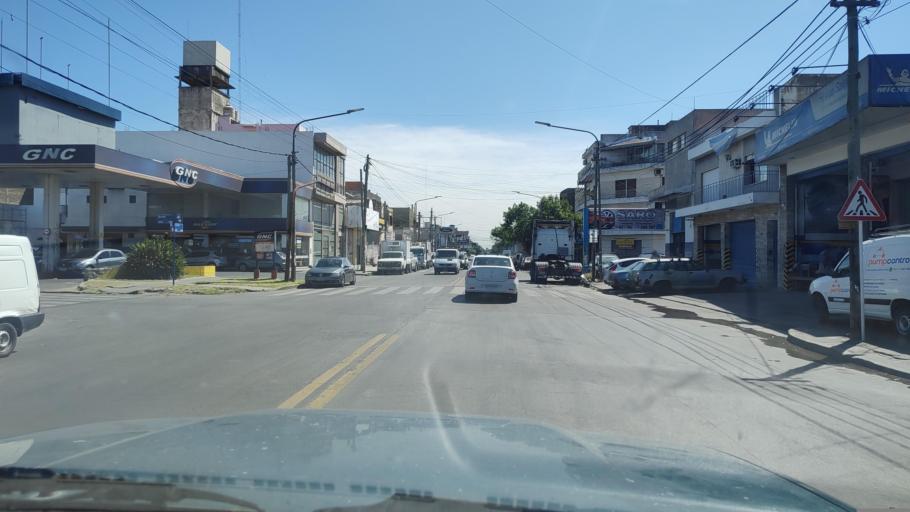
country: AR
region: Buenos Aires
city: San Justo
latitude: -34.6817
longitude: -58.5707
